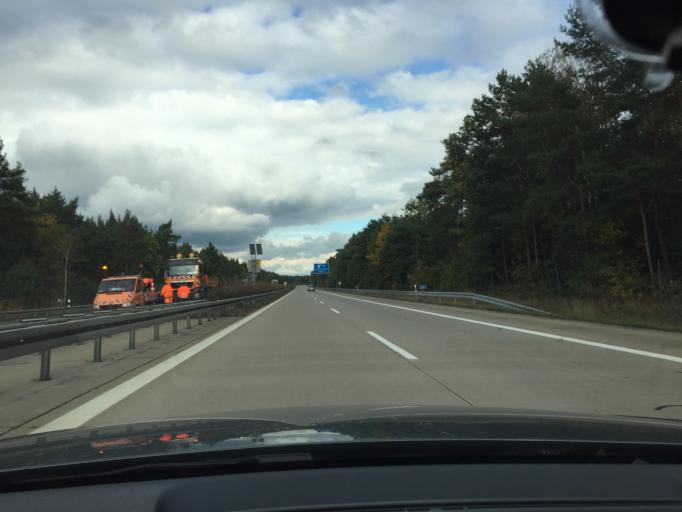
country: DE
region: Brandenburg
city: Schwarzheide
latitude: 51.4792
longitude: 13.8747
